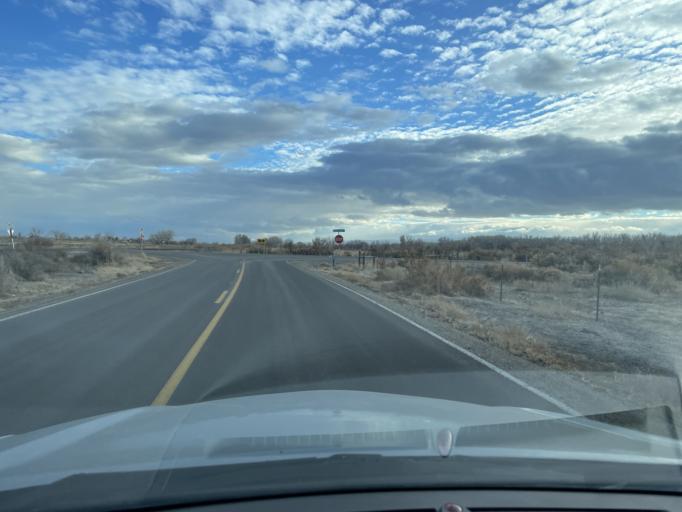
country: US
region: Colorado
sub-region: Montrose County
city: Olathe
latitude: 38.6432
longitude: -107.9937
